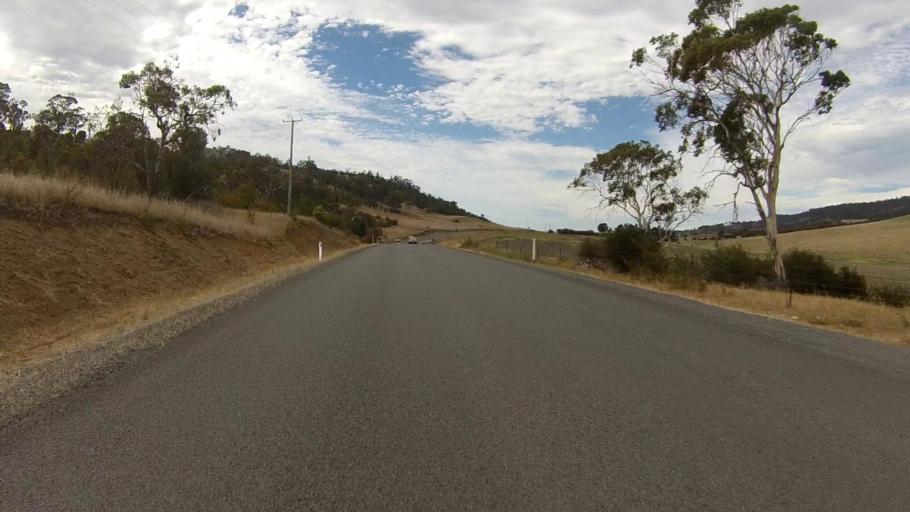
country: AU
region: Tasmania
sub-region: Brighton
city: Old Beach
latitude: -42.7212
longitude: 147.3365
